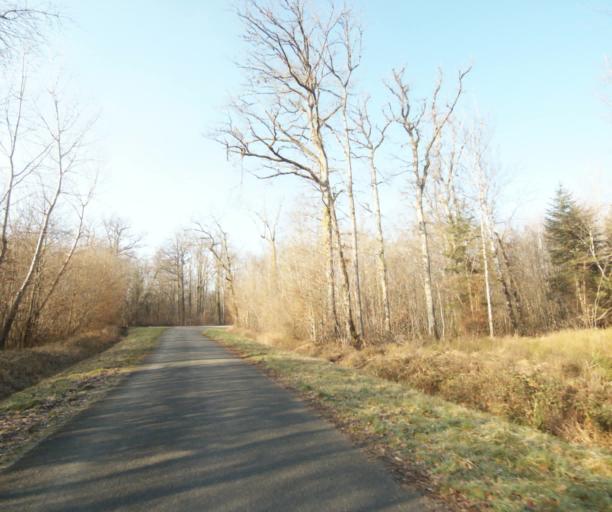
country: FR
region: Champagne-Ardenne
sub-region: Departement de la Haute-Marne
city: Wassy
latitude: 48.4565
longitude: 4.9391
